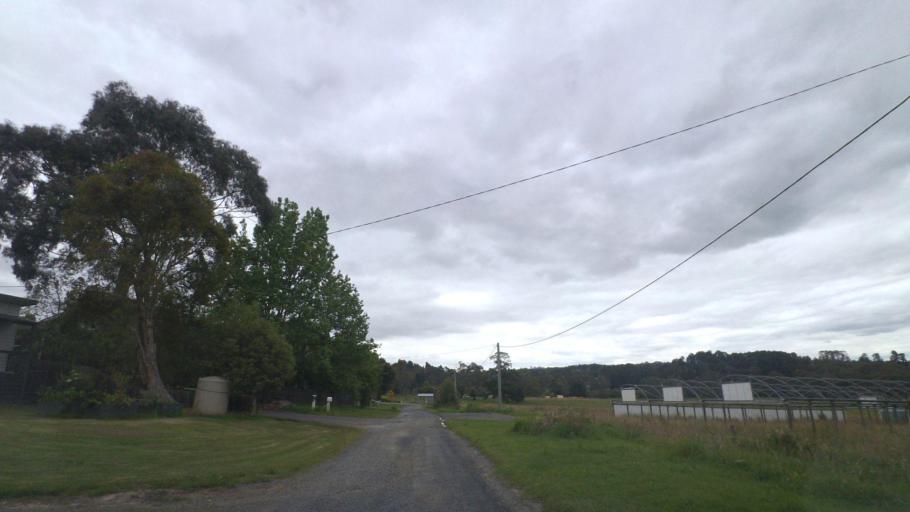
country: AU
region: Victoria
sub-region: Yarra Ranges
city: Mount Evelyn
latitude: -37.7758
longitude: 145.4253
